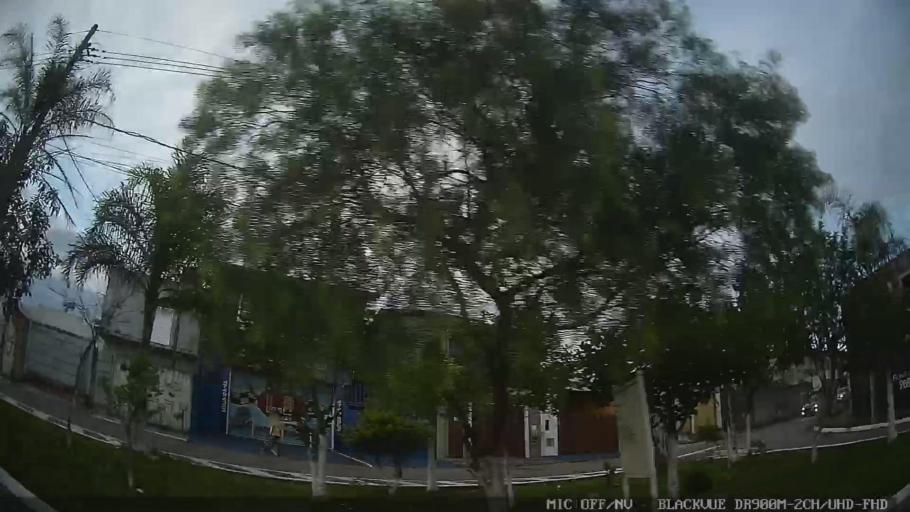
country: BR
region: Sao Paulo
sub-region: Suzano
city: Suzano
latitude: -23.5070
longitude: -46.3038
